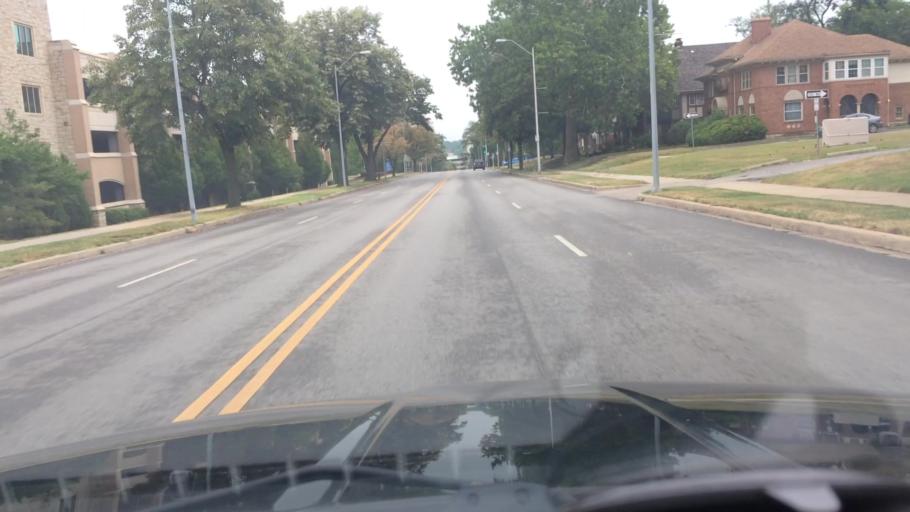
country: US
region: Kansas
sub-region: Johnson County
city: Westwood
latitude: 39.0311
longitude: -94.5759
